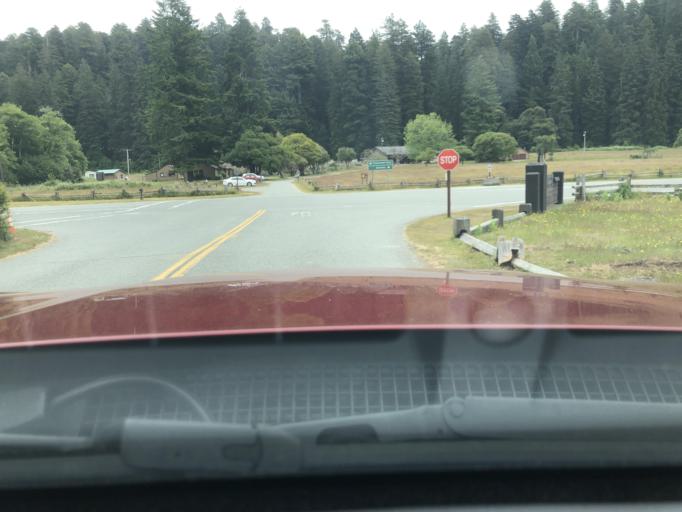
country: US
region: California
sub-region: Humboldt County
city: Westhaven-Moonstone
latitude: 41.3640
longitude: -124.0214
